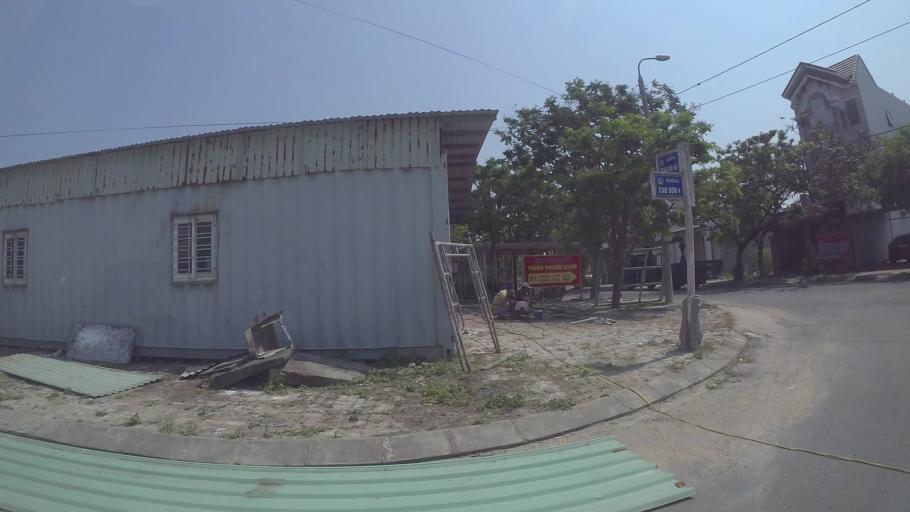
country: VN
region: Da Nang
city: Ngu Hanh Son
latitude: 15.9840
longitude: 108.2725
